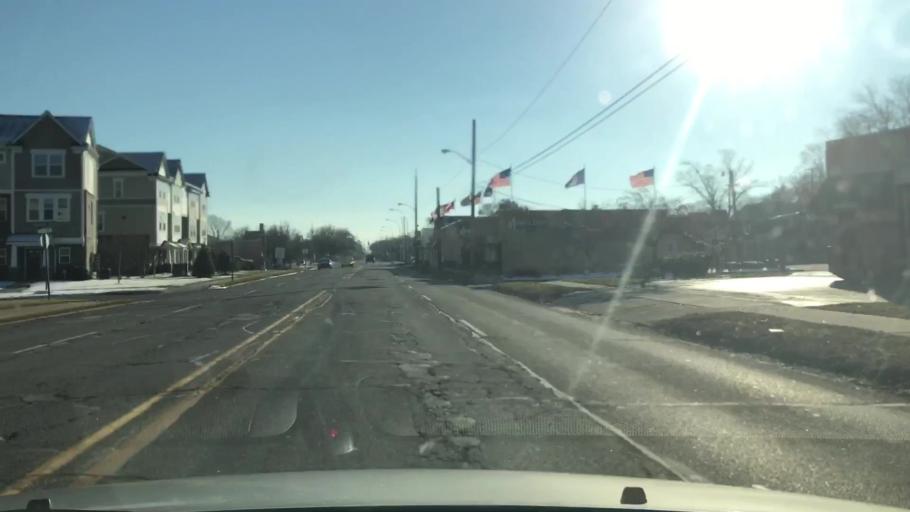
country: US
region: Michigan
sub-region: Oakland County
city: Clawson
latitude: 42.5214
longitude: -83.1389
